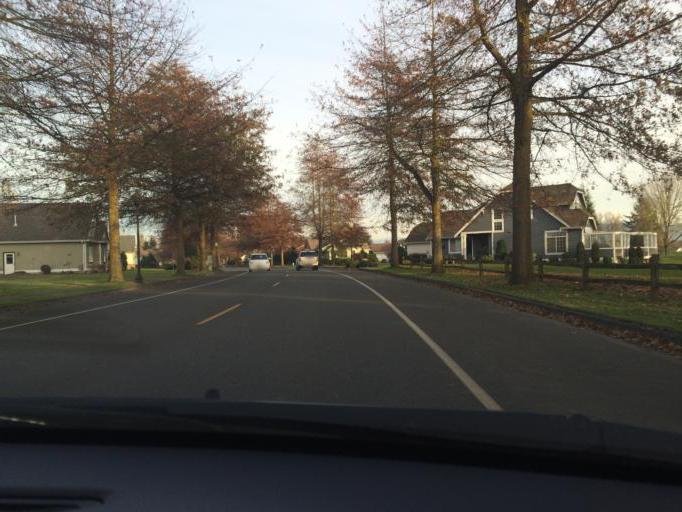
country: US
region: Washington
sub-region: Whatcom County
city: Lynden
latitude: 48.9597
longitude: -122.4497
